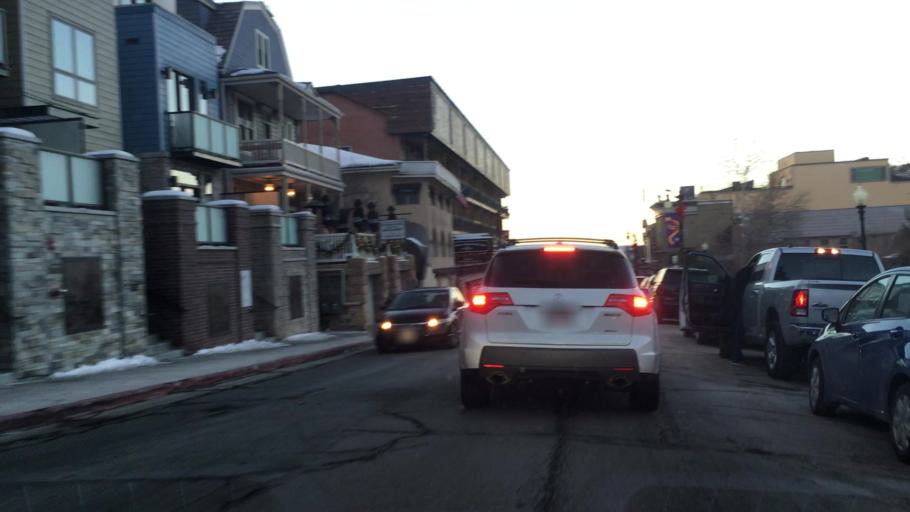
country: US
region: Utah
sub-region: Summit County
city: Park City
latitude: 40.6410
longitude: -111.4944
